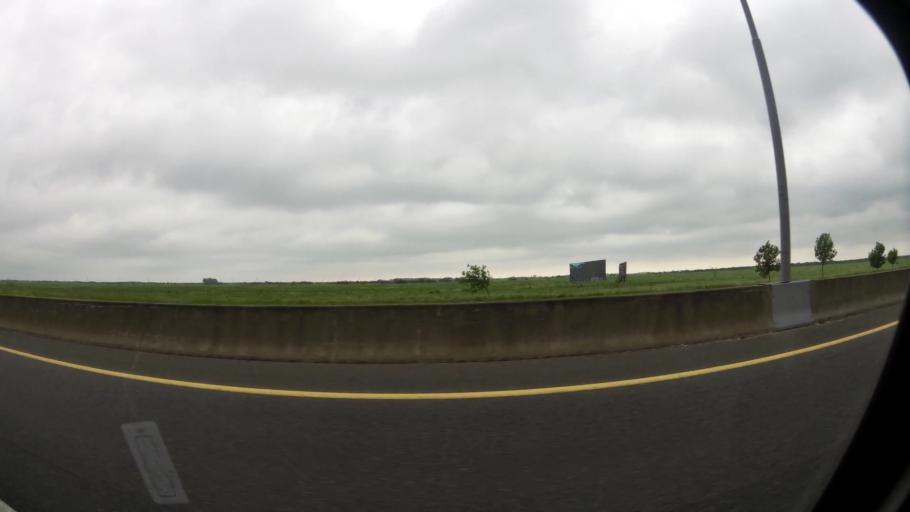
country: AR
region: Buenos Aires
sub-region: Partido de La Plata
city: La Plata
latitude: -34.8543
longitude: -58.0351
